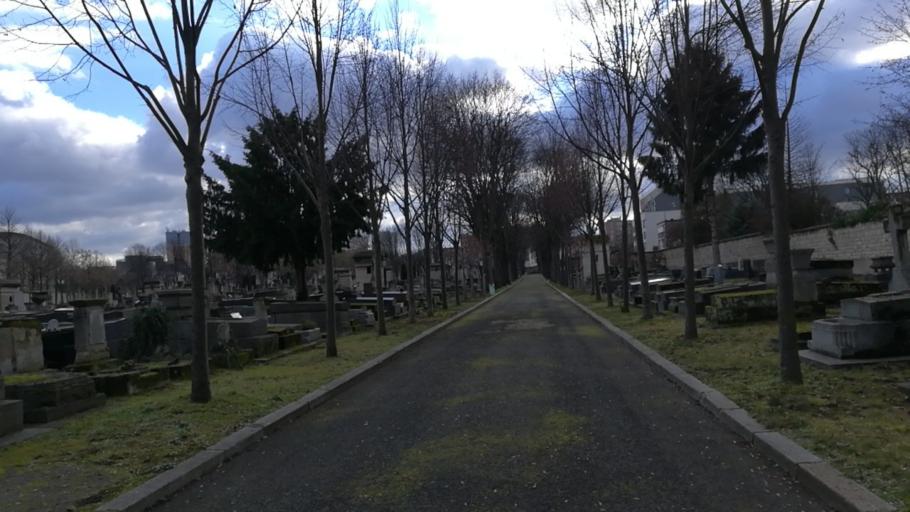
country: FR
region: Ile-de-France
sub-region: Paris
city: Saint-Ouen
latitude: 48.9064
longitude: 2.3509
